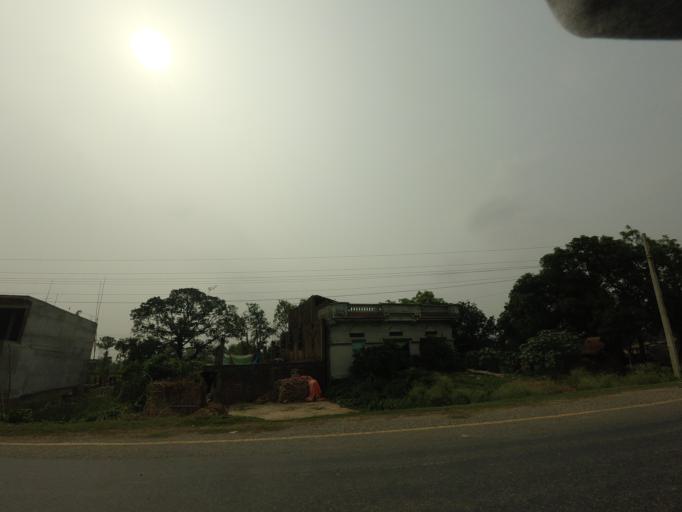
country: IN
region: Uttar Pradesh
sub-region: Maharajganj
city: Nautanwa
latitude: 27.4977
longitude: 83.3293
